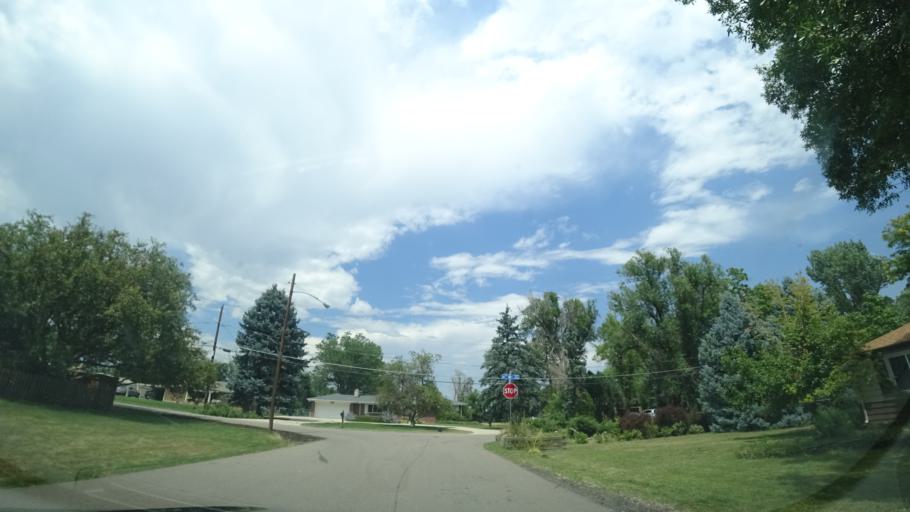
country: US
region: Colorado
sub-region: Jefferson County
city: Lakewood
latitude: 39.7218
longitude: -105.0844
